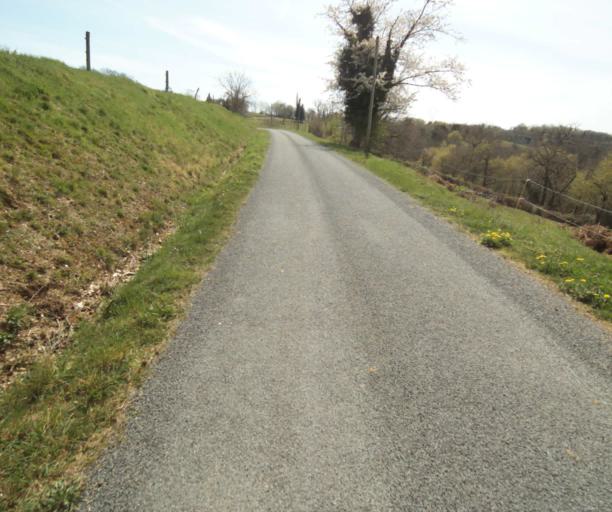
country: FR
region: Limousin
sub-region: Departement de la Correze
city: Naves
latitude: 45.3764
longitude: 1.8017
